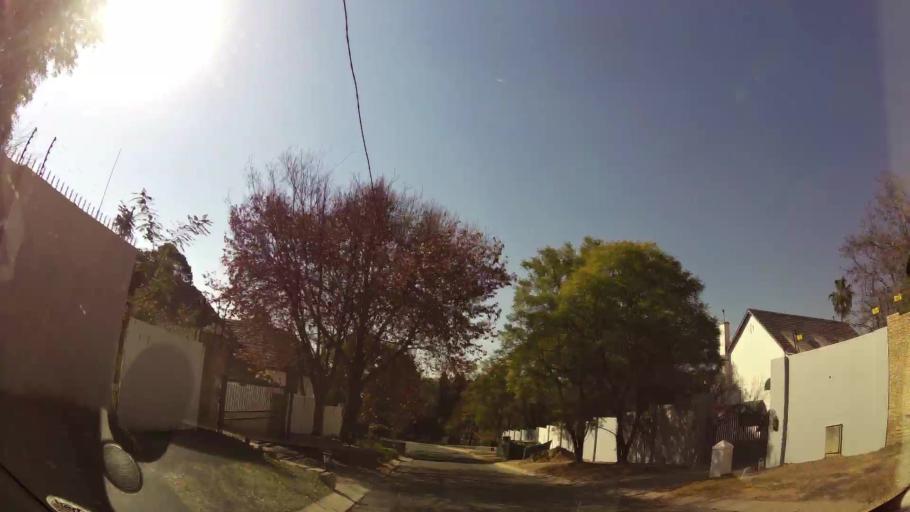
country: ZA
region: Gauteng
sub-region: City of Johannesburg Metropolitan Municipality
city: Johannesburg
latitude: -26.0986
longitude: 28.0298
